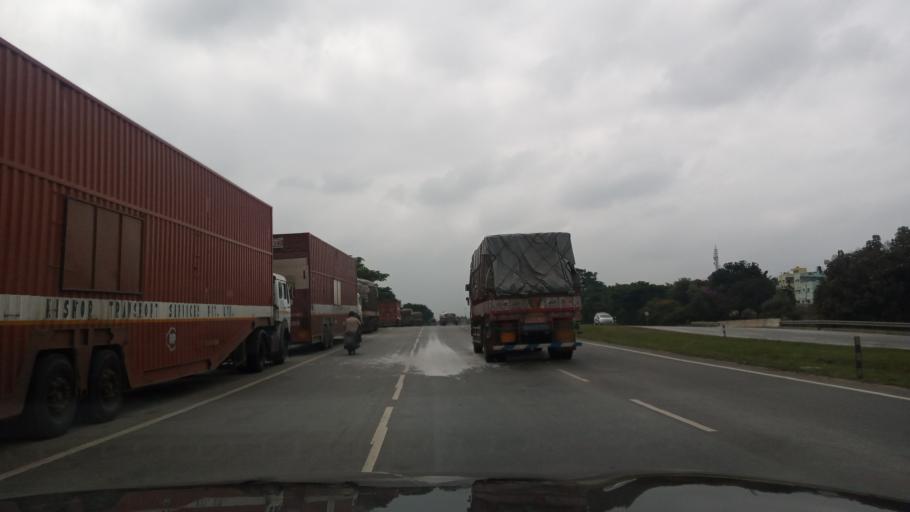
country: IN
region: Karnataka
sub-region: Bangalore Rural
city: Nelamangala
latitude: 13.0528
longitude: 77.4768
